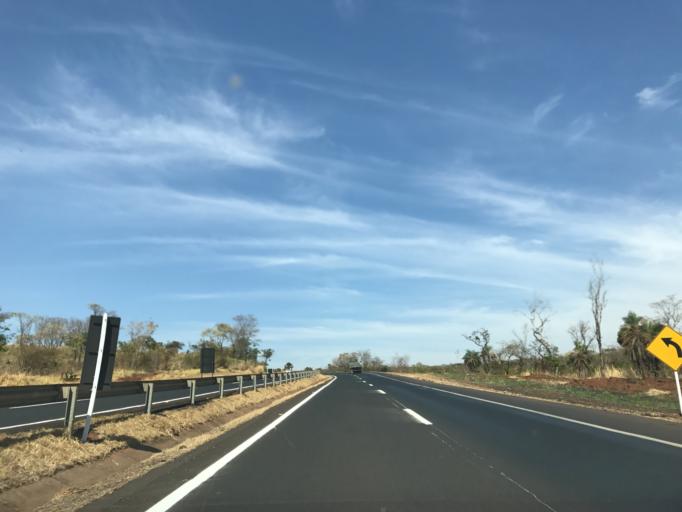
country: BR
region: Minas Gerais
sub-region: Monte Alegre De Minas
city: Monte Alegre de Minas
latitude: -18.8326
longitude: -49.0897
